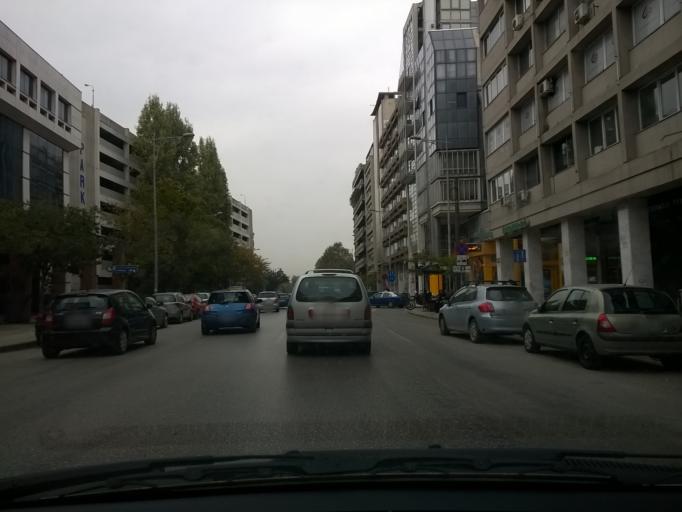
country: GR
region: Central Macedonia
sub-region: Nomos Thessalonikis
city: Thessaloniki
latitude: 40.6370
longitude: 22.9352
